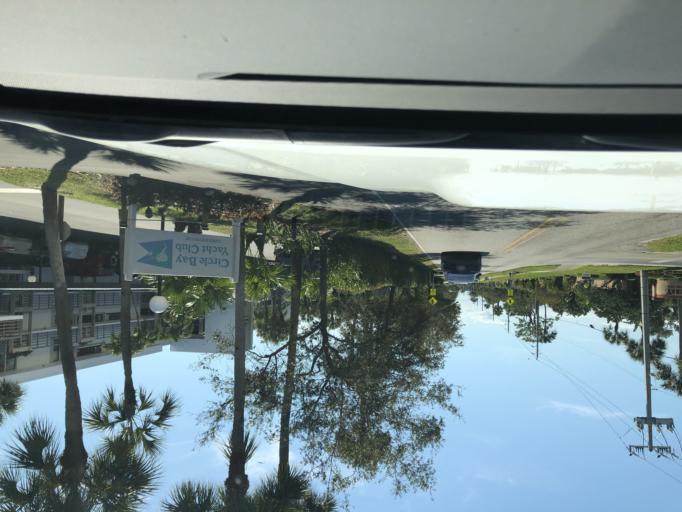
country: US
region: Florida
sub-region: Martin County
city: Palm City
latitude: 27.1797
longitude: -80.2571
